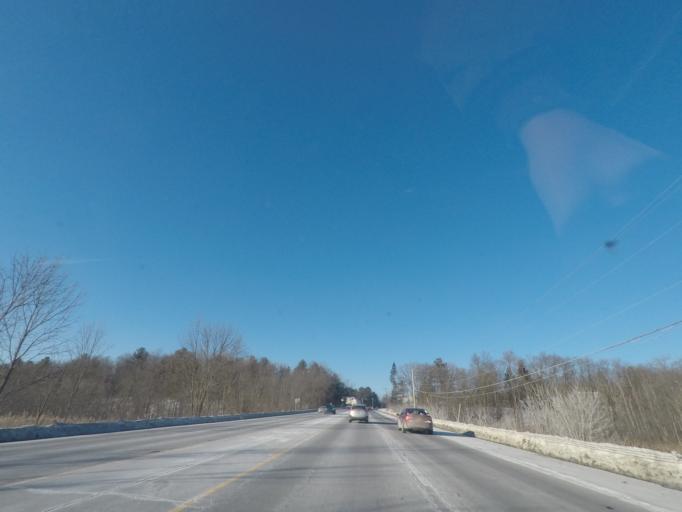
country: US
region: New York
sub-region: Saratoga County
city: Saratoga Springs
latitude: 43.0401
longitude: -73.7903
